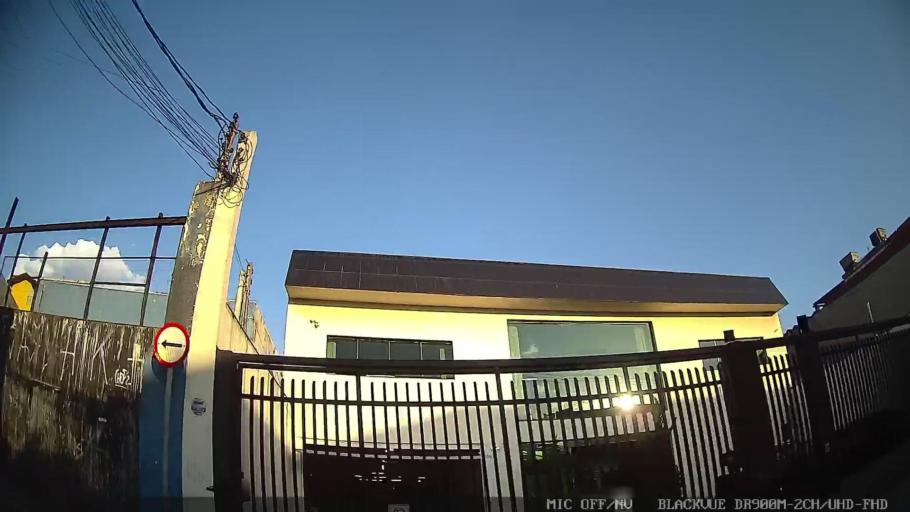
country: BR
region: Sao Paulo
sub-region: Sao Caetano Do Sul
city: Sao Caetano do Sul
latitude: -23.5791
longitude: -46.5492
